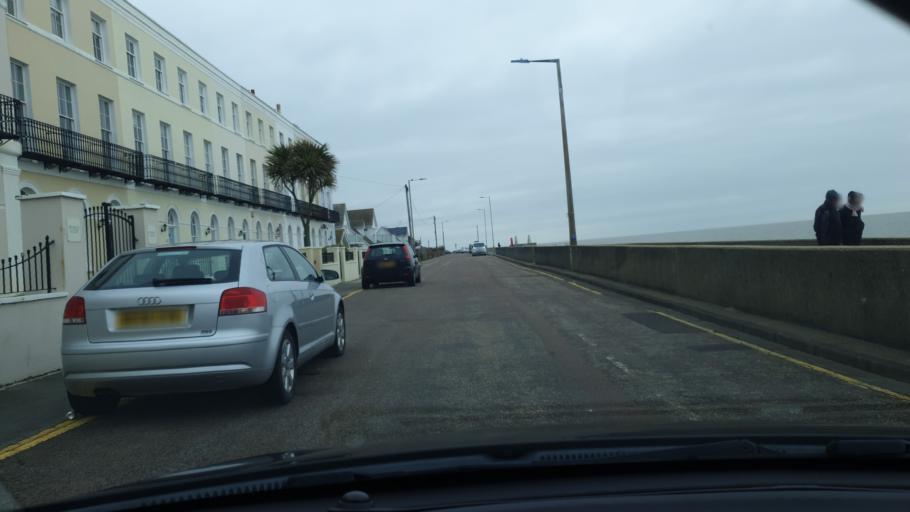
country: GB
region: England
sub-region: Essex
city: Walton-on-the-Naze
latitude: 51.8533
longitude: 1.2784
